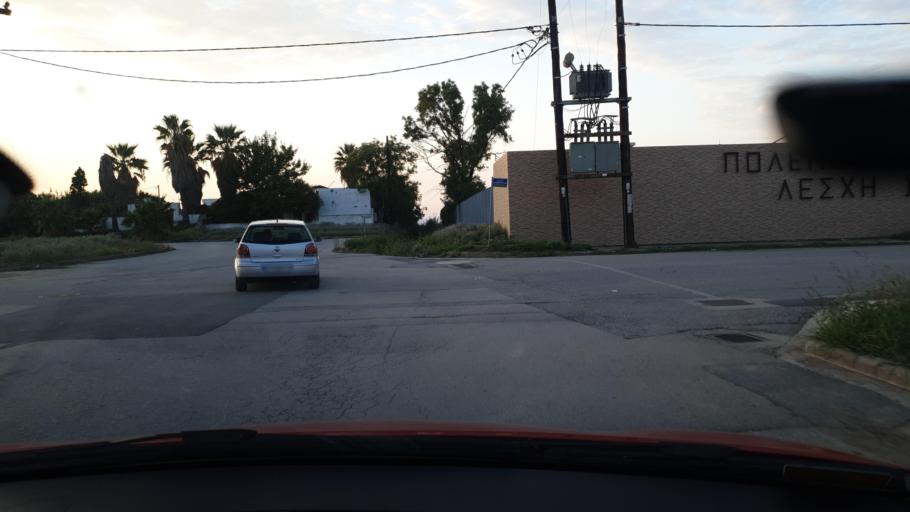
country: GR
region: Central Macedonia
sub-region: Nomos Thessalonikis
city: Peraia
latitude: 40.5109
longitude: 22.9352
